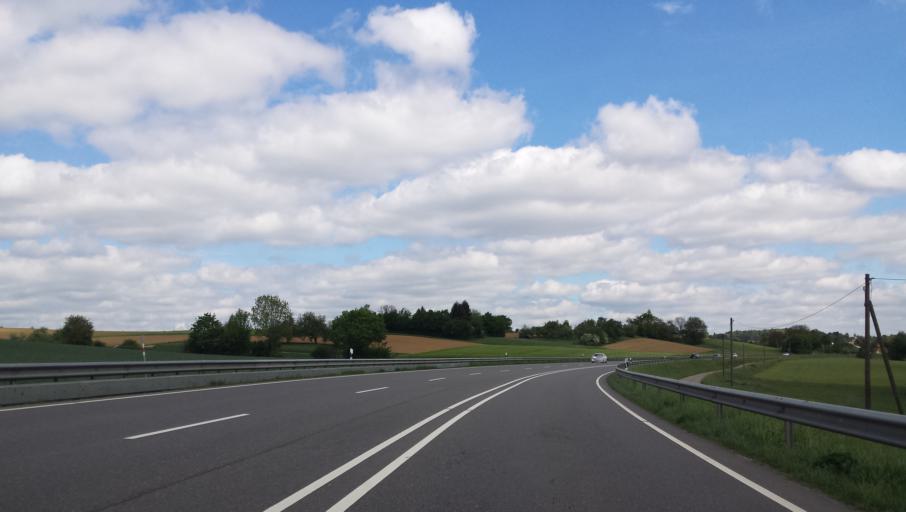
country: DE
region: Baden-Wuerttemberg
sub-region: Karlsruhe Region
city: Aglasterhausen
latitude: 49.3452
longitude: 8.9786
